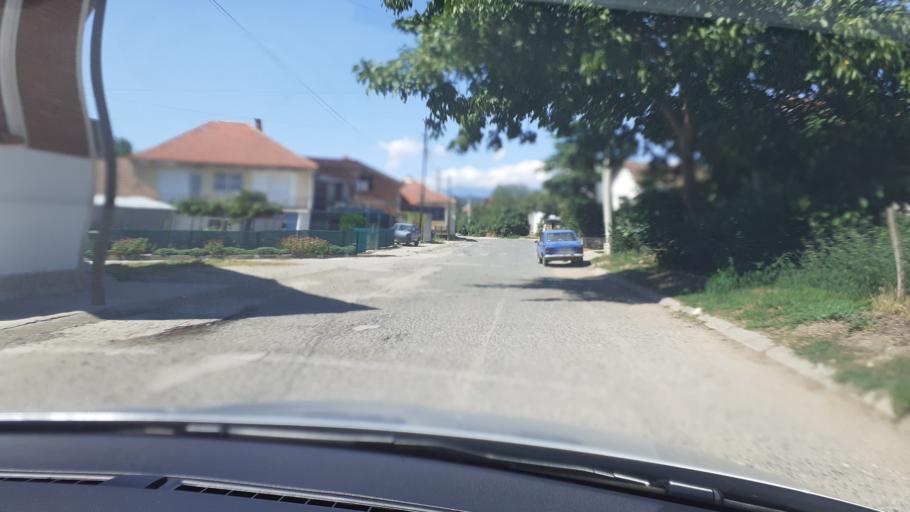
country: MK
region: Bogdanci
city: Bogdanci
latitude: 41.2002
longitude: 22.5782
